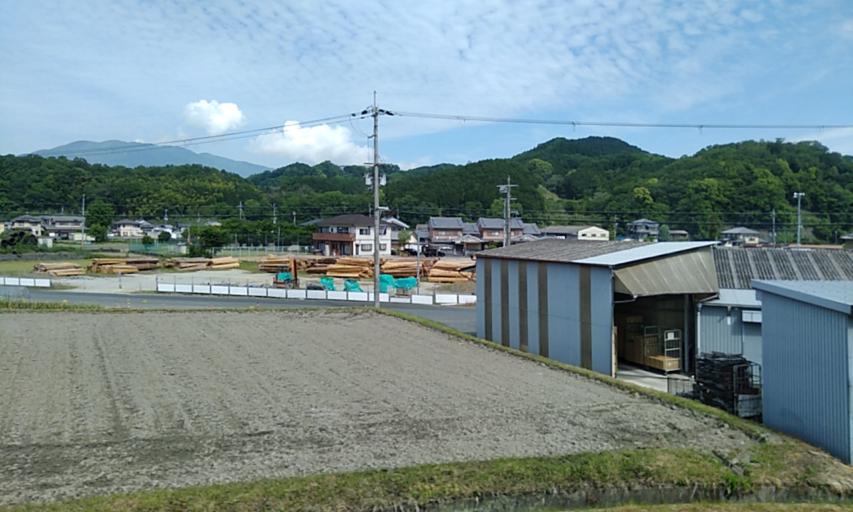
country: JP
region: Nara
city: Gose
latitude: 34.4363
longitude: 135.7645
